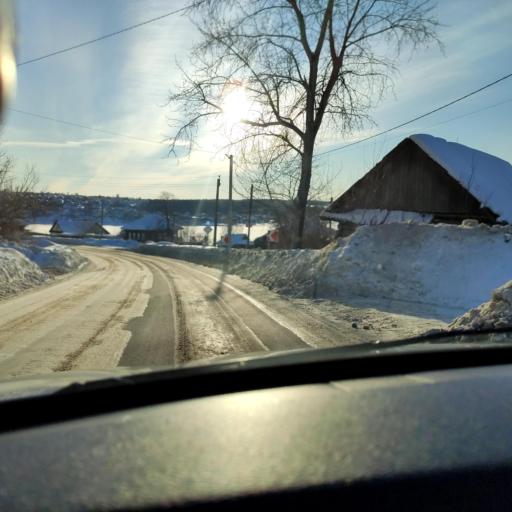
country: RU
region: Perm
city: Polazna
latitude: 58.3104
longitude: 56.4229
